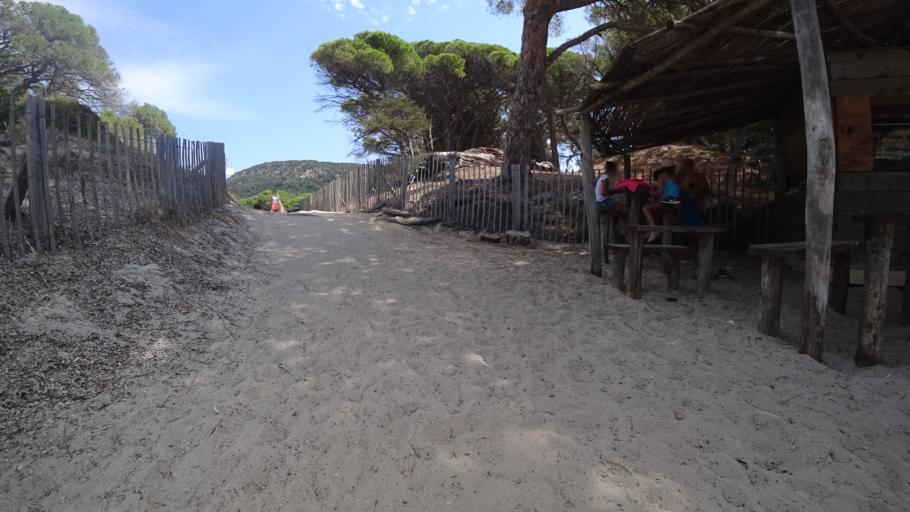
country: FR
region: Corsica
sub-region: Departement de la Corse-du-Sud
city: Porto-Vecchio
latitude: 41.5597
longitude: 9.3361
